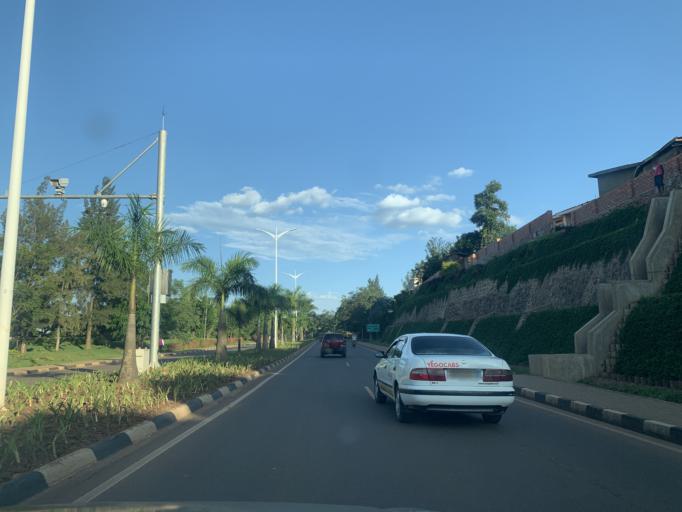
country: RW
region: Kigali
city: Kigali
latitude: -1.9631
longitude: 30.1258
